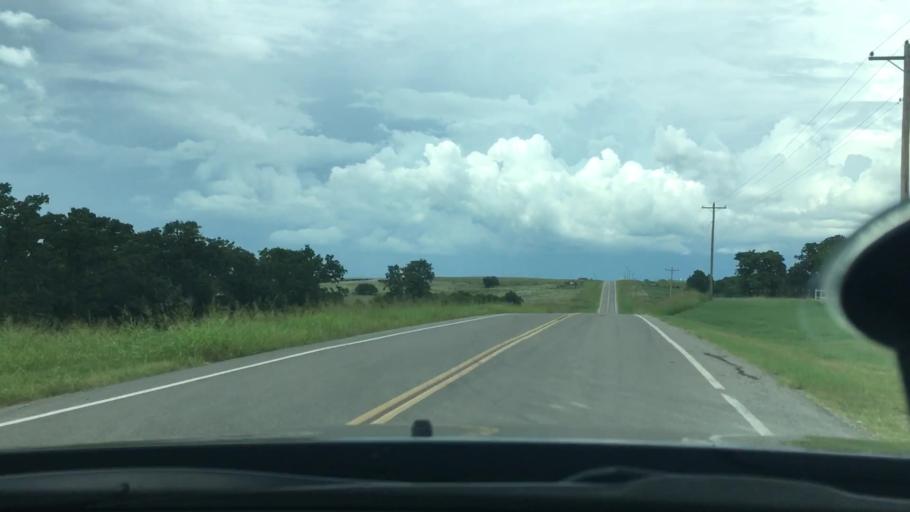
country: US
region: Oklahoma
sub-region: Garvin County
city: Stratford
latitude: 34.8110
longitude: -97.0554
